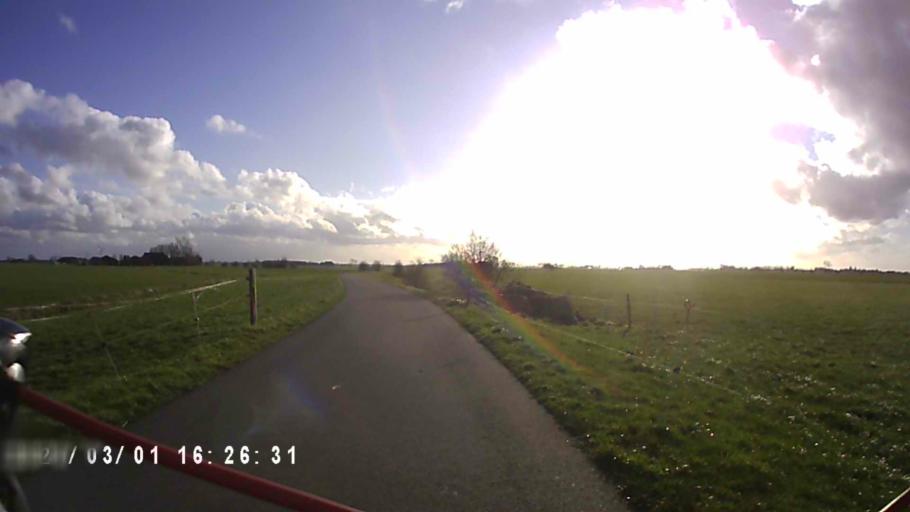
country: NL
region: Groningen
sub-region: Gemeente Zuidhorn
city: Oldehove
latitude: 53.3086
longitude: 6.4288
